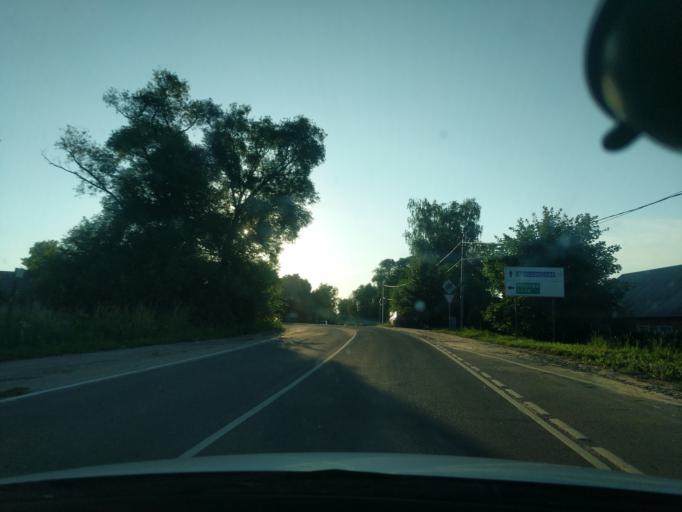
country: RU
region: Moskovskaya
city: Serpukhov
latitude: 54.8599
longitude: 37.4770
